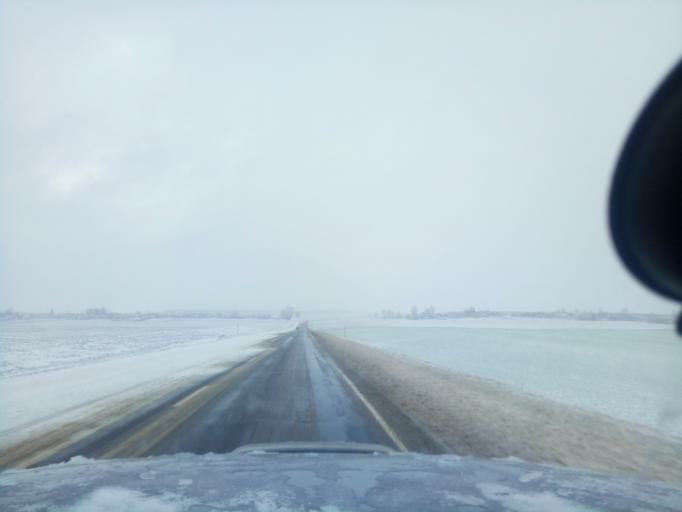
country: BY
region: Minsk
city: Haradzyeya
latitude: 53.3078
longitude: 26.5698
